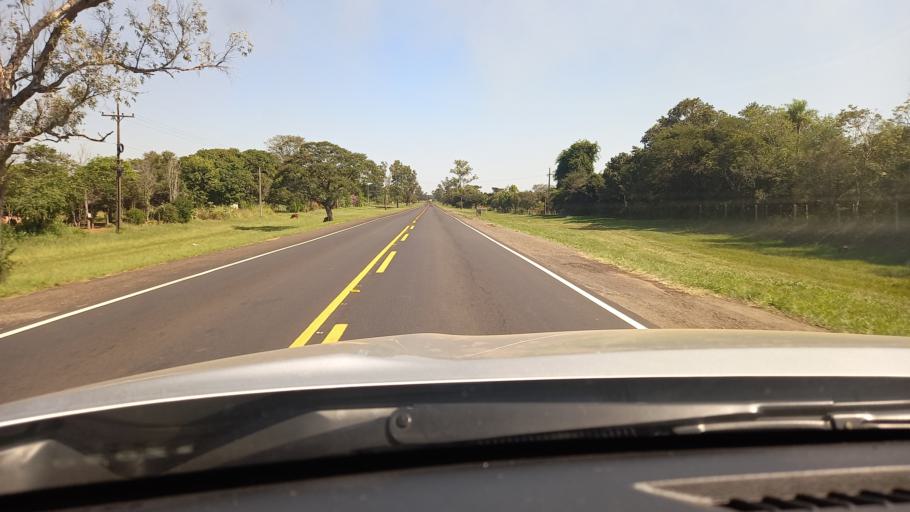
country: PY
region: Itapua
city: General Delgado
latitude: -27.0874
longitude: -56.4941
